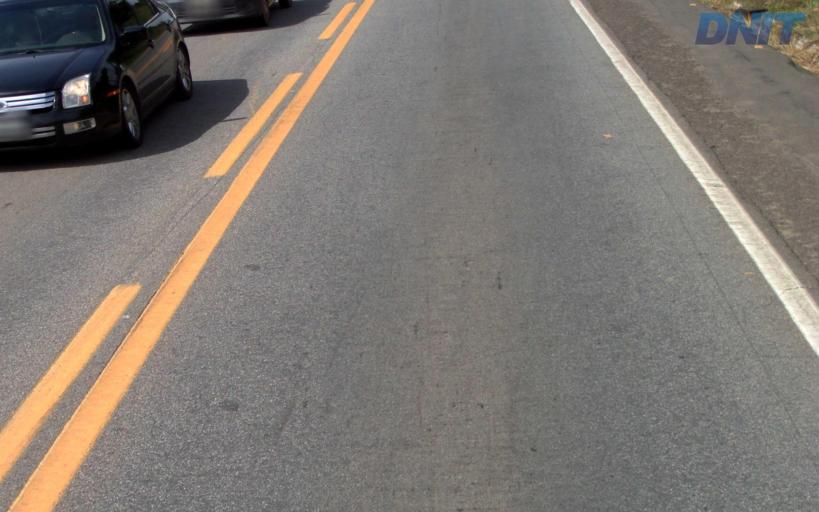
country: BR
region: Minas Gerais
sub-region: Ipatinga
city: Ipatinga
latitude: -19.4273
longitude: -42.5014
